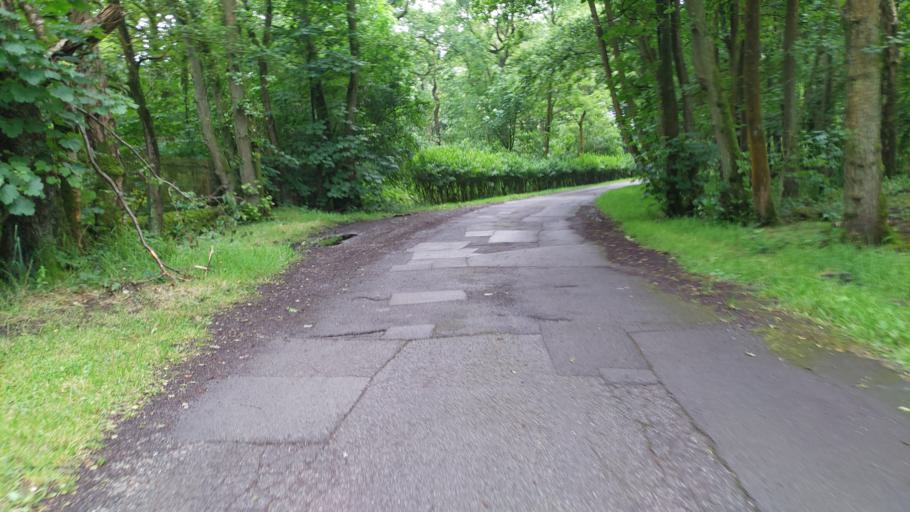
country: GB
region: England
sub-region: Lancashire
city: Chorley
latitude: 53.6830
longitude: -2.5700
